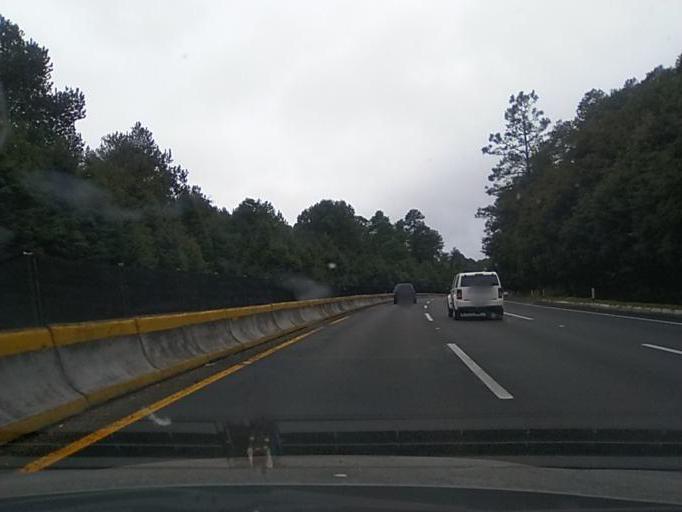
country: MX
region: Morelos
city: Tres Marias
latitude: 19.1081
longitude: -99.1871
